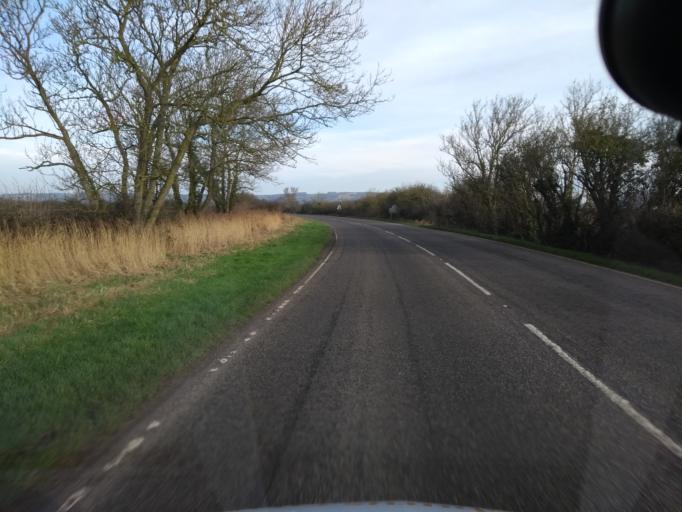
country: GB
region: England
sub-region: North Somerset
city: Bleadon
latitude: 51.2674
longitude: -2.9346
